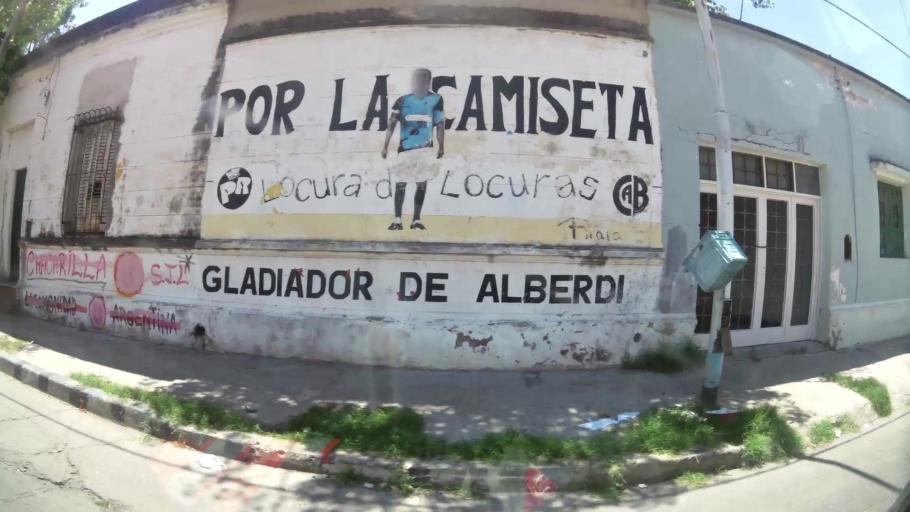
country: AR
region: Cordoba
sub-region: Departamento de Capital
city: Cordoba
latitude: -31.4049
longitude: -64.2054
